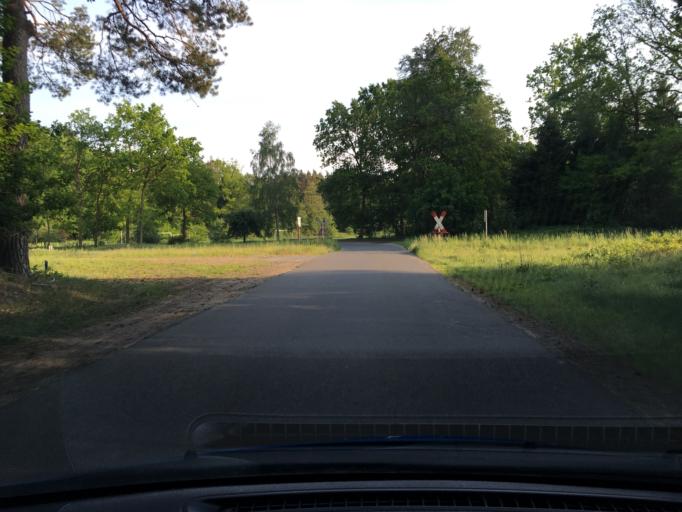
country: DE
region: Lower Saxony
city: Ludersburg
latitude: 53.2866
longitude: 10.5688
